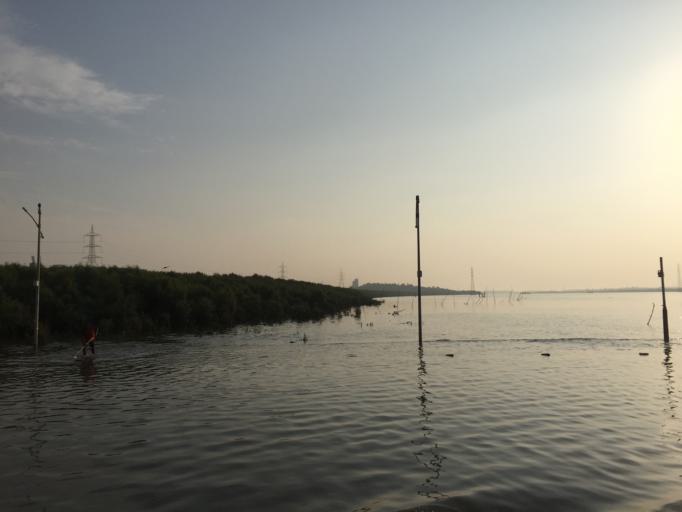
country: IN
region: Maharashtra
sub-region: Mumbai Suburban
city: Borivli
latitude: 19.2342
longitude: 72.8229
